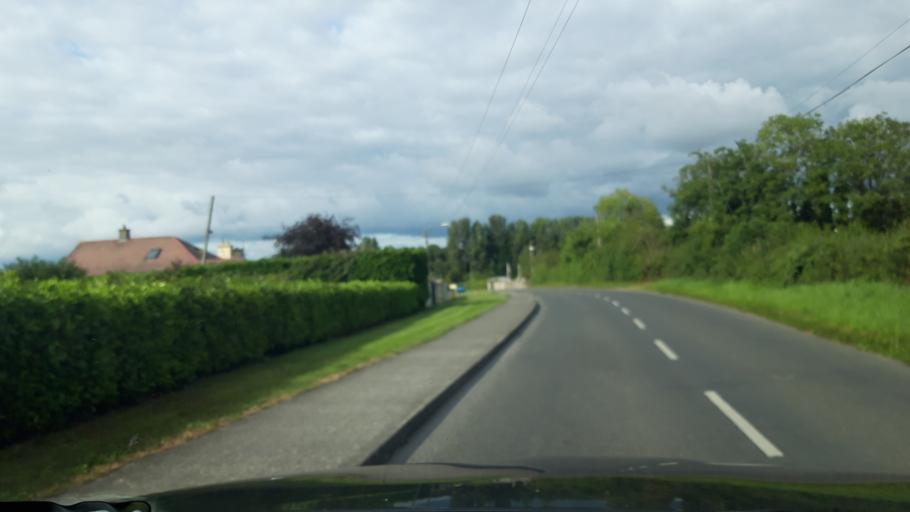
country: IE
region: Leinster
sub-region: Kildare
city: Athy
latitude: 53.0035
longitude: -6.9642
